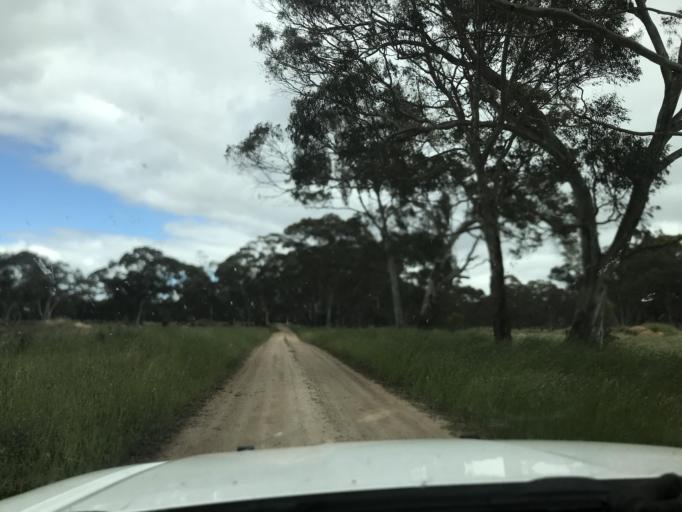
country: AU
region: South Australia
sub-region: Wattle Range
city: Penola
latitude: -37.1219
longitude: 141.2197
